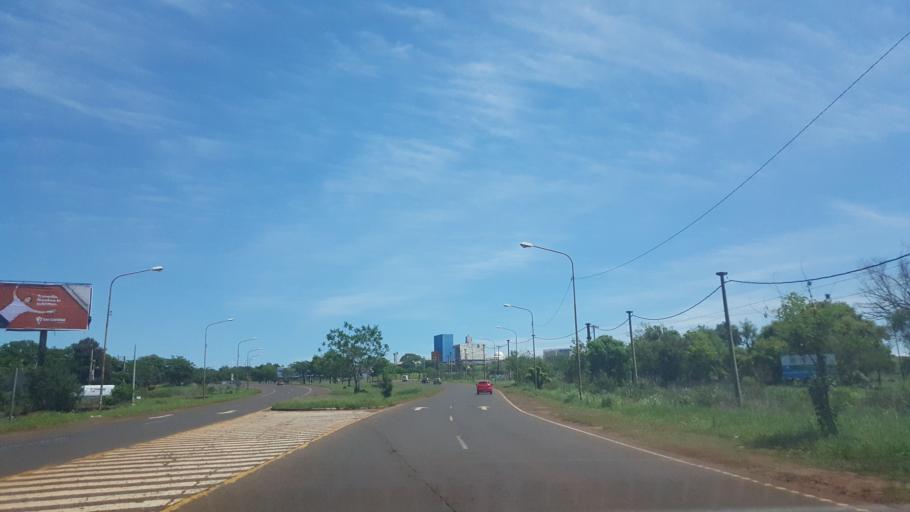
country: AR
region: Misiones
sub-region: Departamento de Capital
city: Posadas
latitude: -27.3985
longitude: -55.9565
